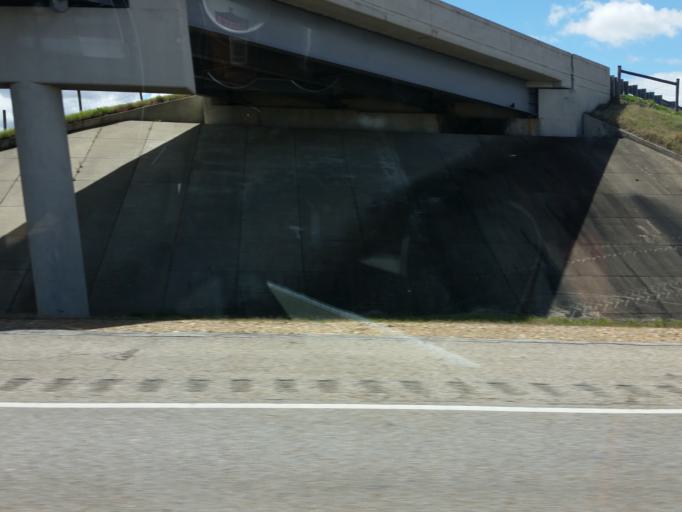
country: US
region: Arkansas
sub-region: Craighead County
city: Bay
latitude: 35.7059
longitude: -90.5670
